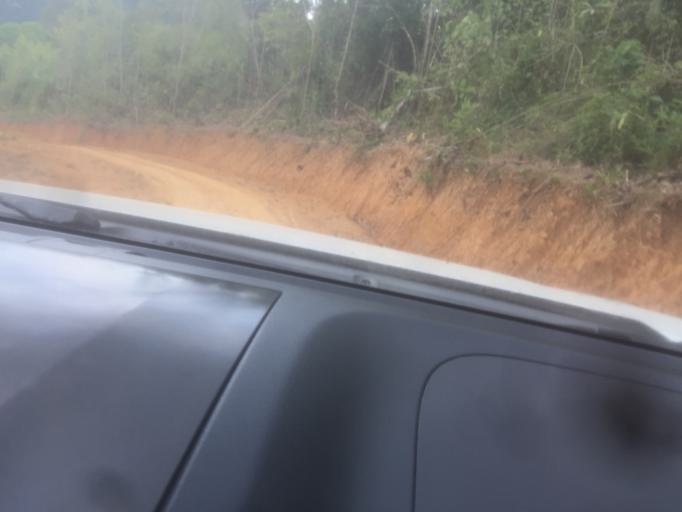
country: LA
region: Phongsali
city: Khoa
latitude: 20.9177
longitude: 102.5602
